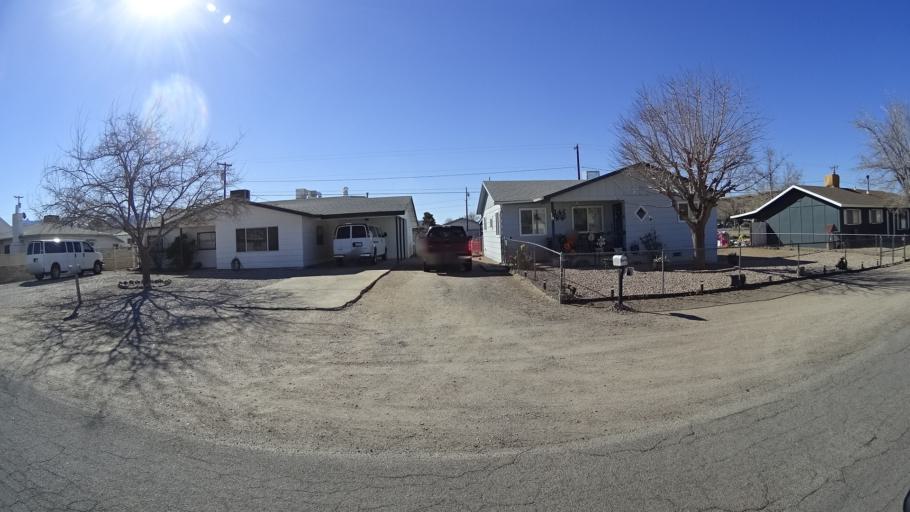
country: US
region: Arizona
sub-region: Mohave County
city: Kingman
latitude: 35.2068
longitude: -114.0302
